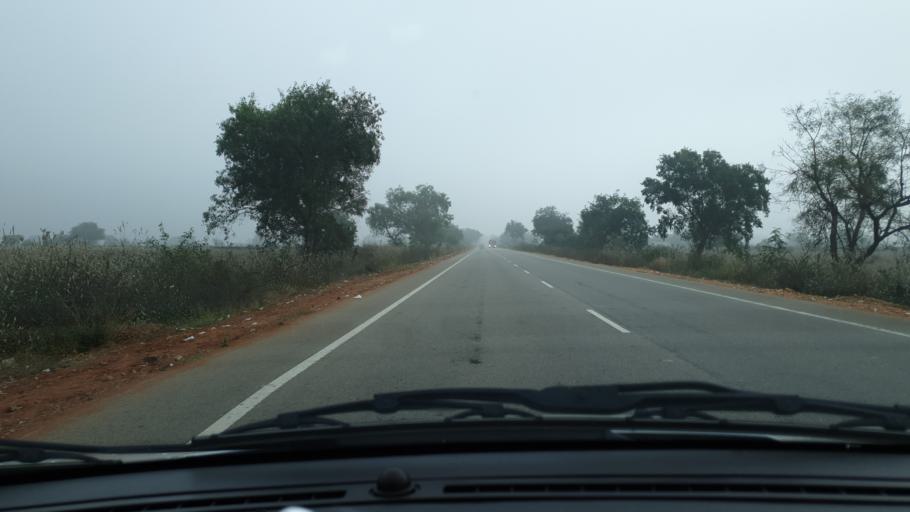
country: IN
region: Telangana
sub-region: Nalgonda
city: Devarkonda
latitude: 16.6364
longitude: 78.6221
